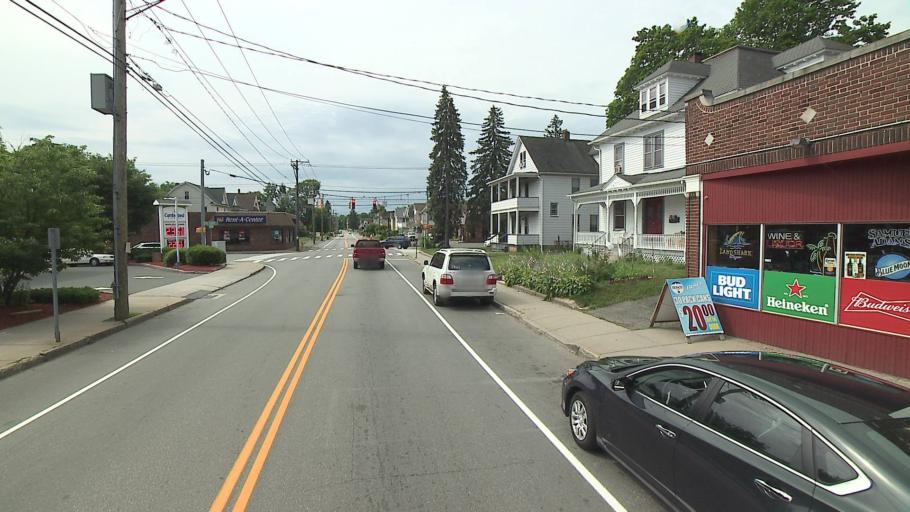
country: US
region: Connecticut
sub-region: Litchfield County
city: Torrington
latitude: 41.7961
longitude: -73.1207
